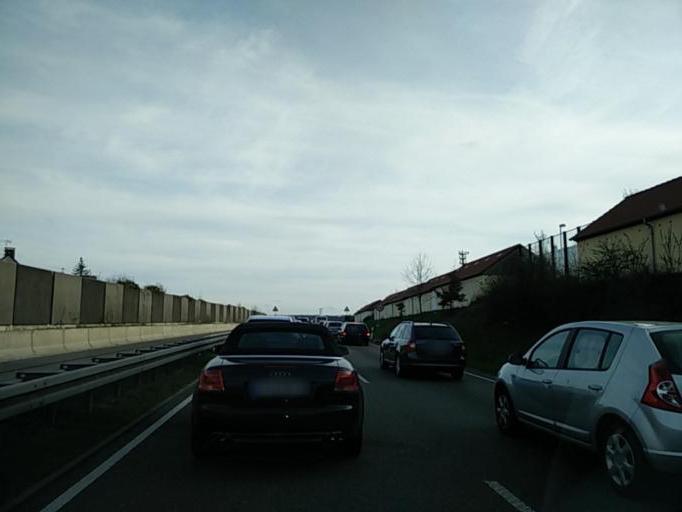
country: DE
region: Baden-Wuerttemberg
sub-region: Regierungsbezirk Stuttgart
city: Holzgerlingen
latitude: 48.6436
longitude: 9.0080
